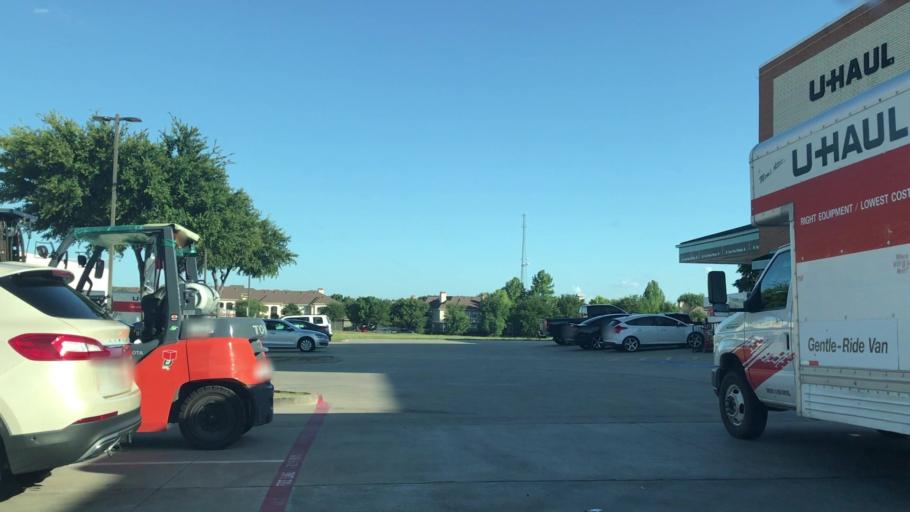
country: US
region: Texas
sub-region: Collin County
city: Allen
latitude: 33.1213
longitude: -96.7412
